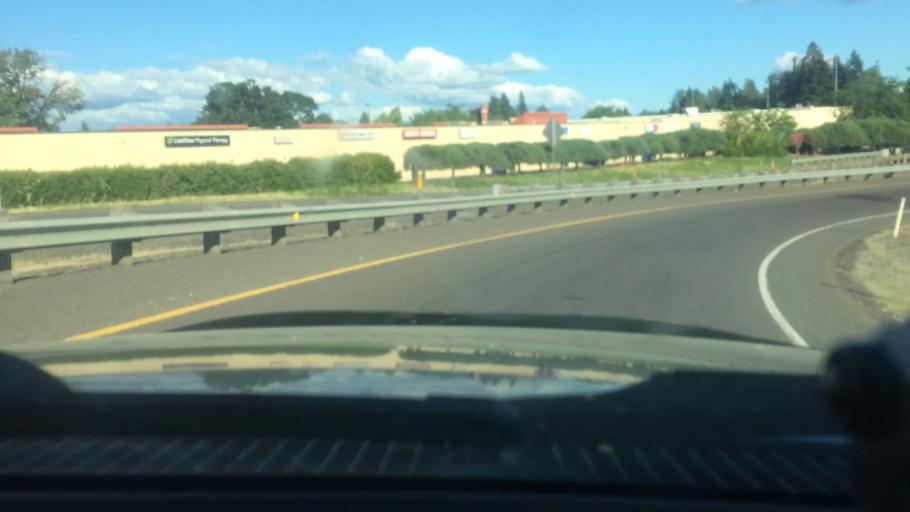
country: US
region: Oregon
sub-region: Lane County
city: Eugene
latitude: 44.0922
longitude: -123.0980
